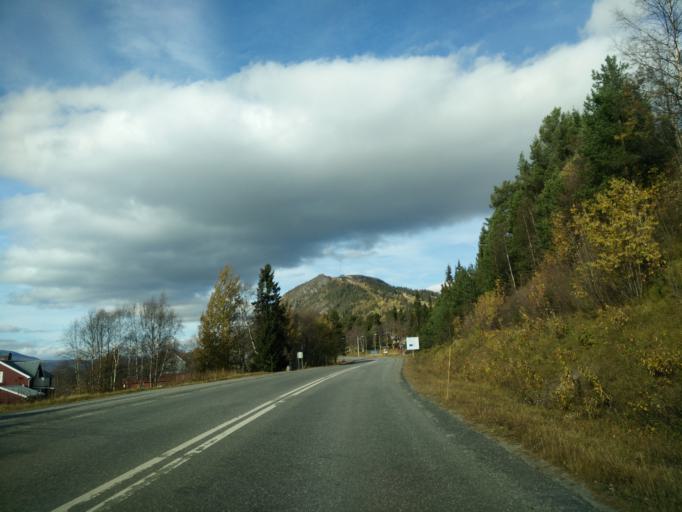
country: NO
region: Hedmark
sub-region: Engerdal
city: Engerdal
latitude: 62.5348
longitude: 12.5586
